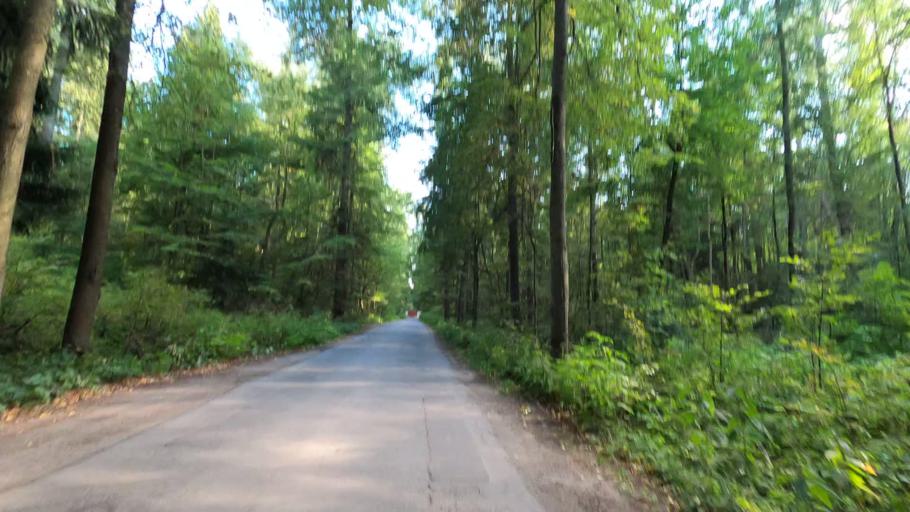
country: RU
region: Moskovskaya
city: Peski
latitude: 55.1776
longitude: 38.7432
